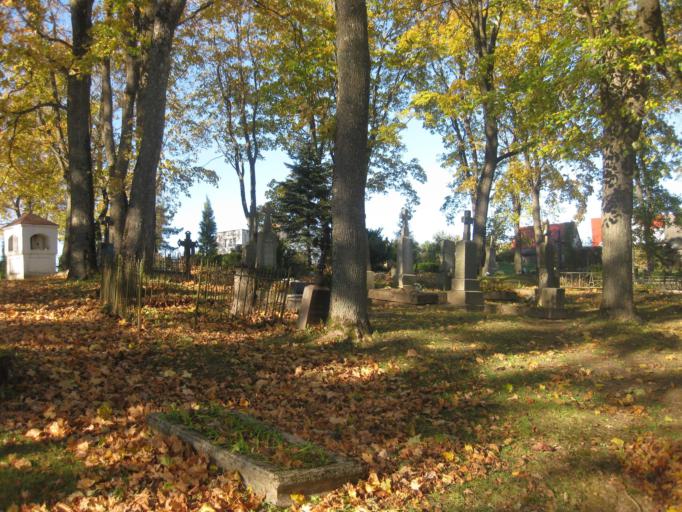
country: LT
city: Vilkija
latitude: 55.0400
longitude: 23.5891
